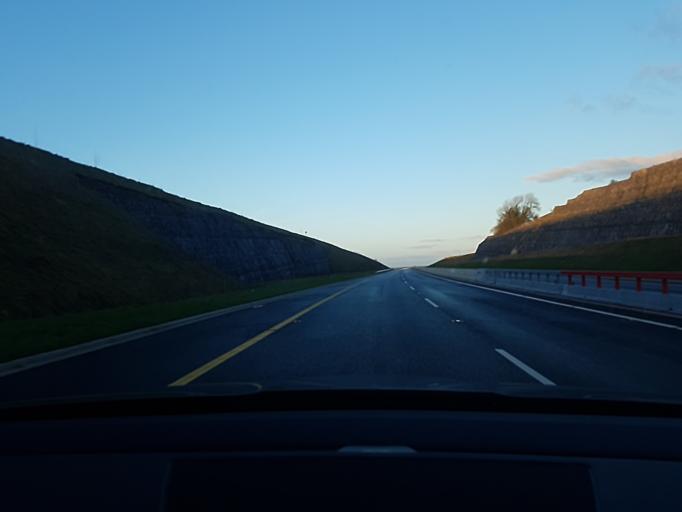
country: IE
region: Connaught
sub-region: County Galway
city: Tuam
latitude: 53.4484
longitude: -8.8497
